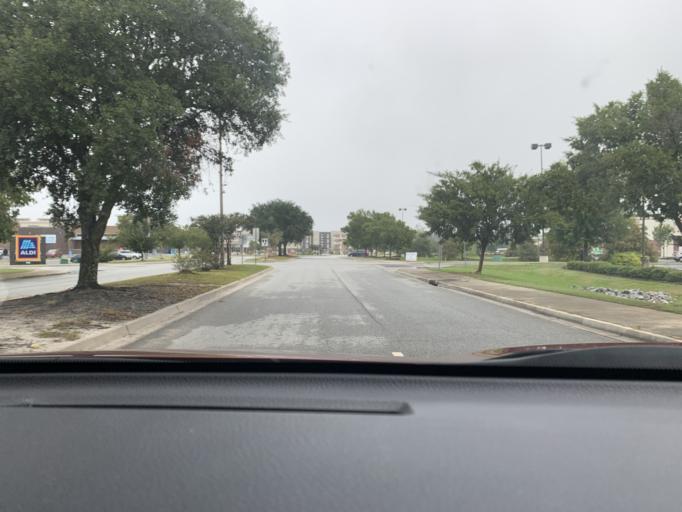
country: US
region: Georgia
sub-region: Chatham County
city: Pooler
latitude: 32.1404
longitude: -81.2515
